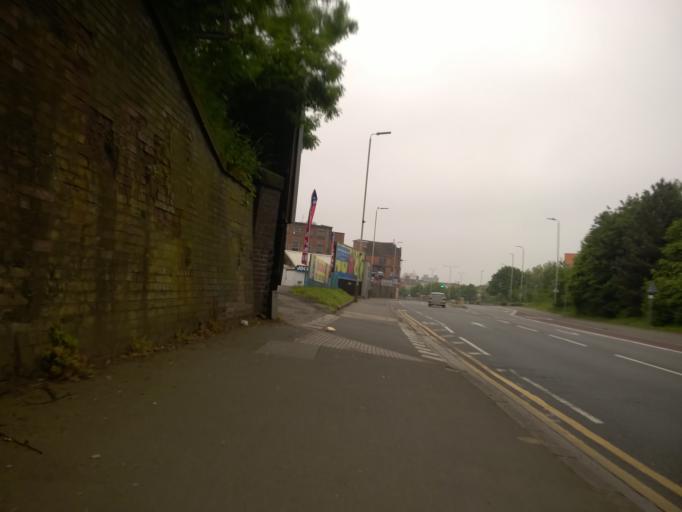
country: GB
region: England
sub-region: City of Leicester
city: Leicester
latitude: 52.6402
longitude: -1.1156
